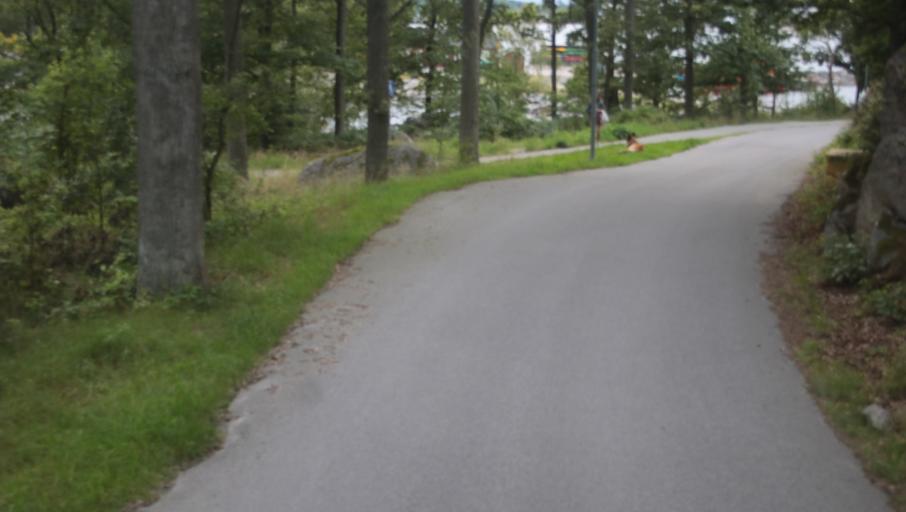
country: SE
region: Blekinge
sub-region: Karlshamns Kommun
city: Karlshamn
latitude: 56.1573
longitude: 14.8798
